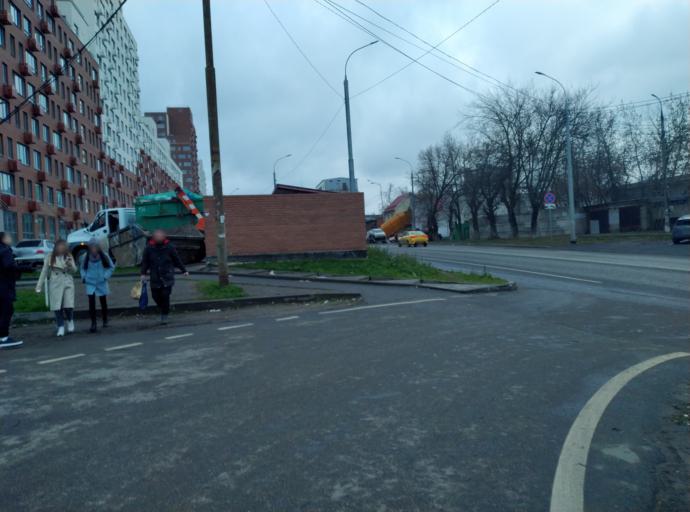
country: RU
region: Moskovskaya
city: Korenevo
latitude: 55.6663
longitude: 37.9978
